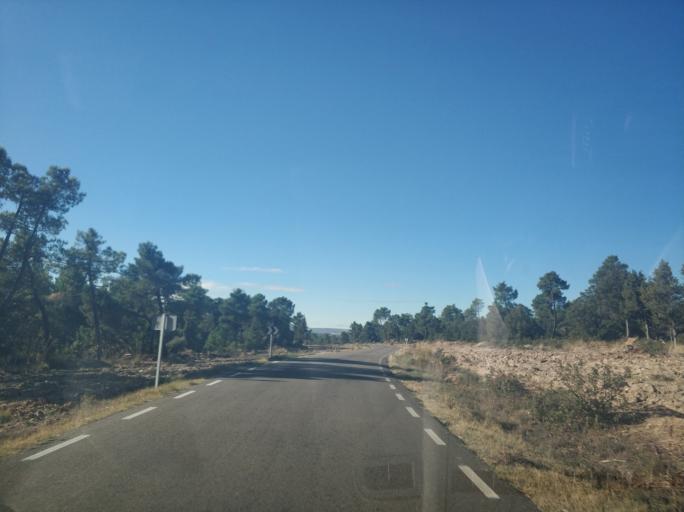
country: ES
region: Castille and Leon
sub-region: Provincia de Burgos
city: San Juan del Monte
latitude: 41.6637
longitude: -3.5308
